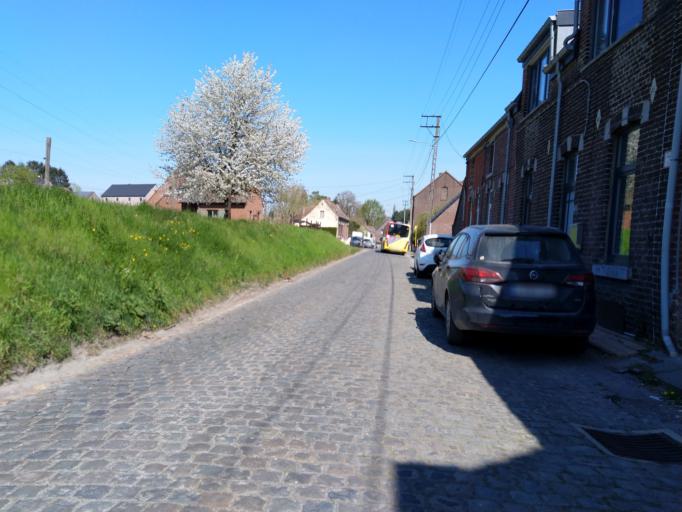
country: BE
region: Wallonia
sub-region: Province du Hainaut
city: Mons
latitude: 50.4790
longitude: 4.0089
